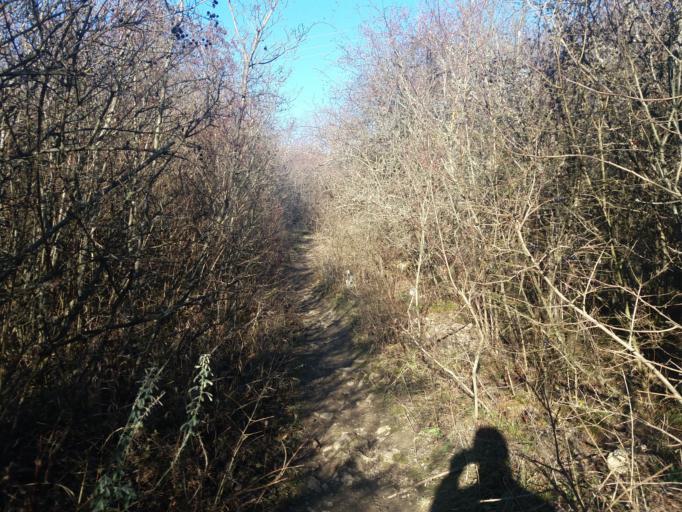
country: HU
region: Pest
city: Budaors
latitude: 47.4703
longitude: 18.9492
